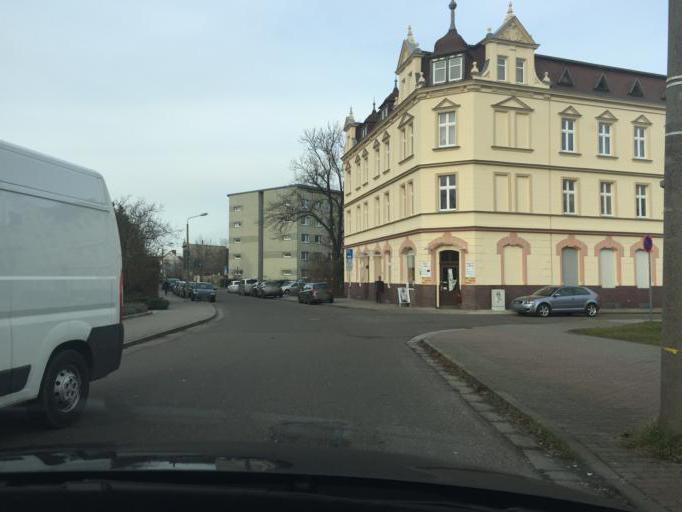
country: DE
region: Brandenburg
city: Cottbus
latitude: 51.7630
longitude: 14.3258
